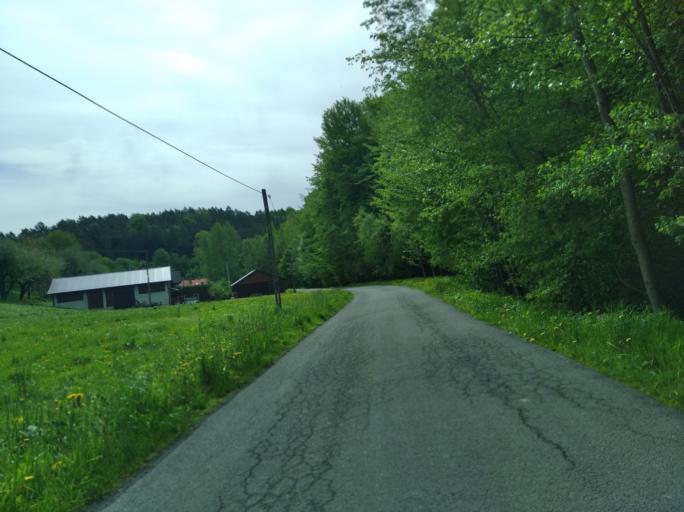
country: PL
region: Subcarpathian Voivodeship
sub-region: Powiat strzyzowski
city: Strzyzow
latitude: 49.9266
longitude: 21.7497
